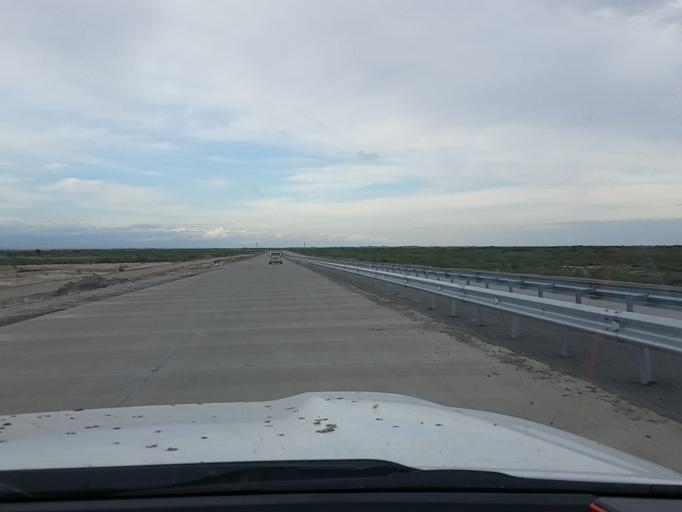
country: KZ
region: Almaty Oblysy
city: Zharkent
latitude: 44.0502
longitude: 79.9965
